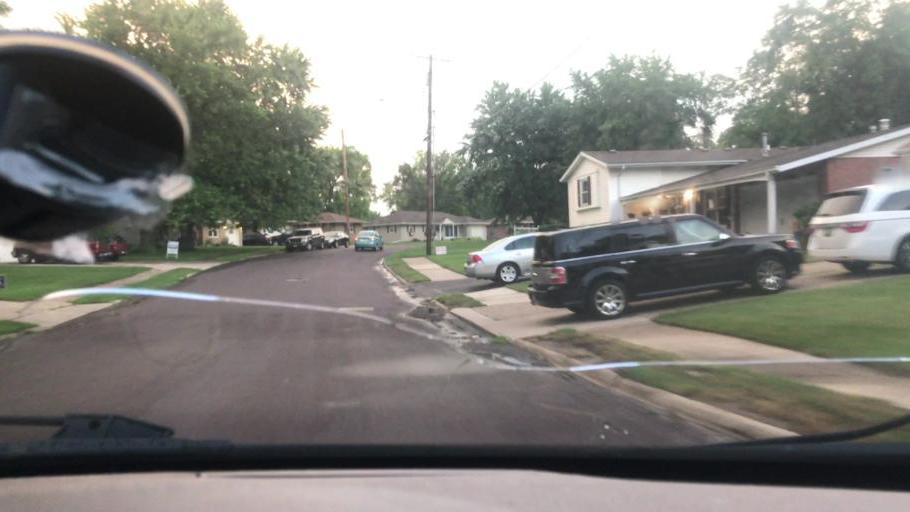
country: US
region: Illinois
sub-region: Tazewell County
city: Pekin
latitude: 40.5477
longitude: -89.6140
